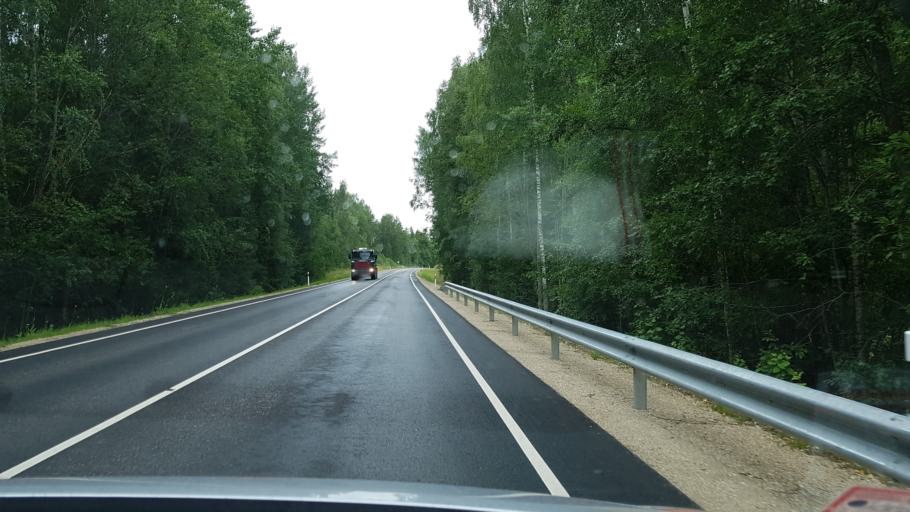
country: EE
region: Polvamaa
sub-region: Raepina vald
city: Rapina
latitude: 58.0790
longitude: 27.2995
